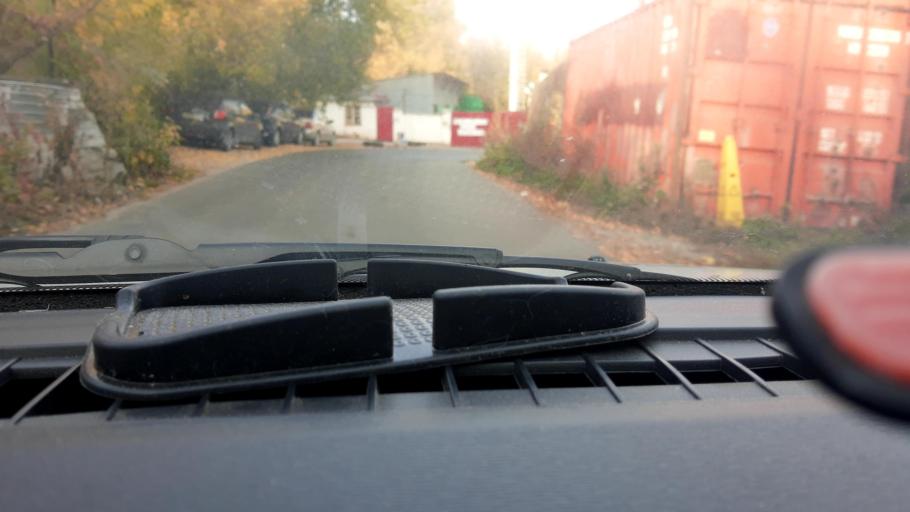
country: RU
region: Nizjnij Novgorod
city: Nizhniy Novgorod
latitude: 56.2527
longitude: 43.9776
